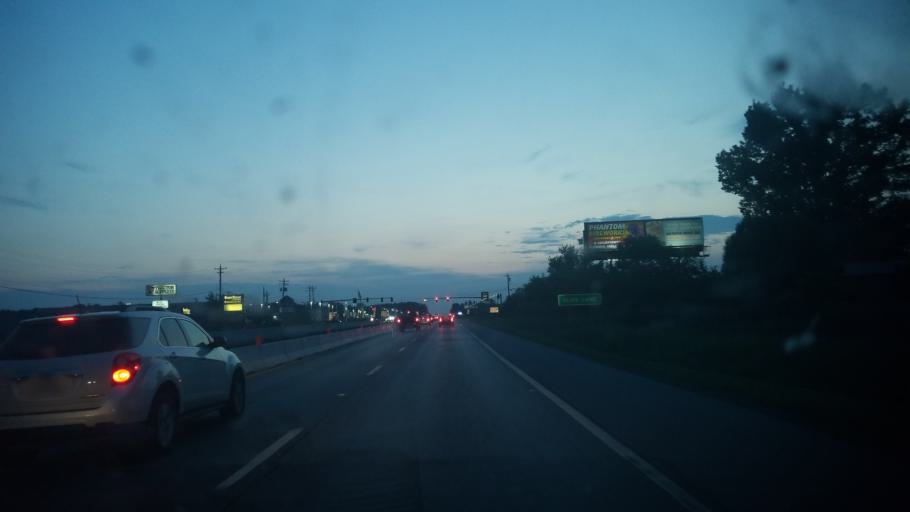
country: US
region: Ohio
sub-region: Clermont County
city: Summerside
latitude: 39.0902
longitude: -84.2457
